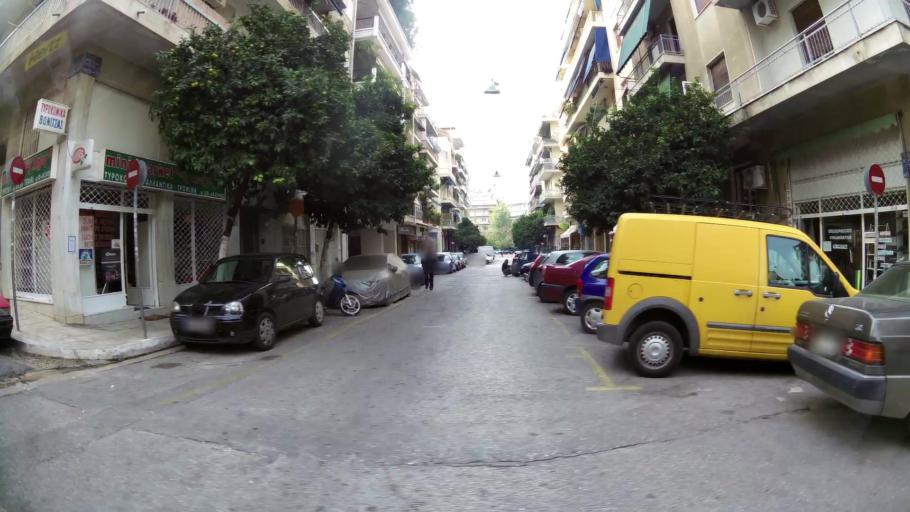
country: GR
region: Attica
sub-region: Nomarchia Athinas
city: Kipseli
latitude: 37.9909
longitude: 23.7434
